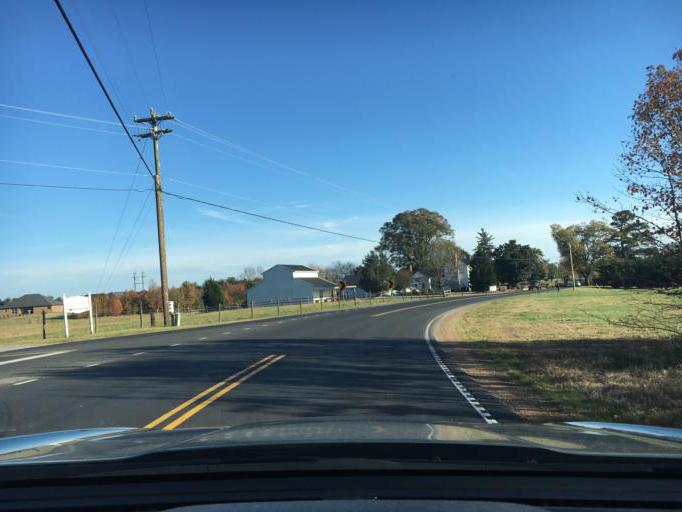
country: US
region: South Carolina
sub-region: Spartanburg County
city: Inman
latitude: 35.0239
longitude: -82.0856
